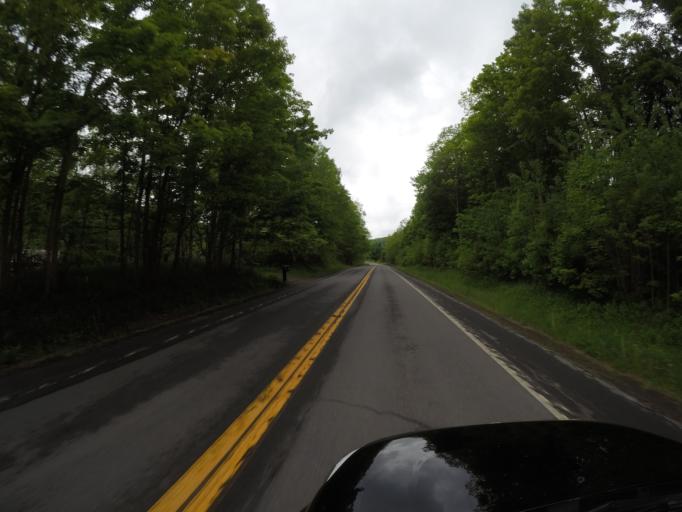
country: US
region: New York
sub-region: Delaware County
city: Delhi
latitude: 42.2588
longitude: -74.8768
